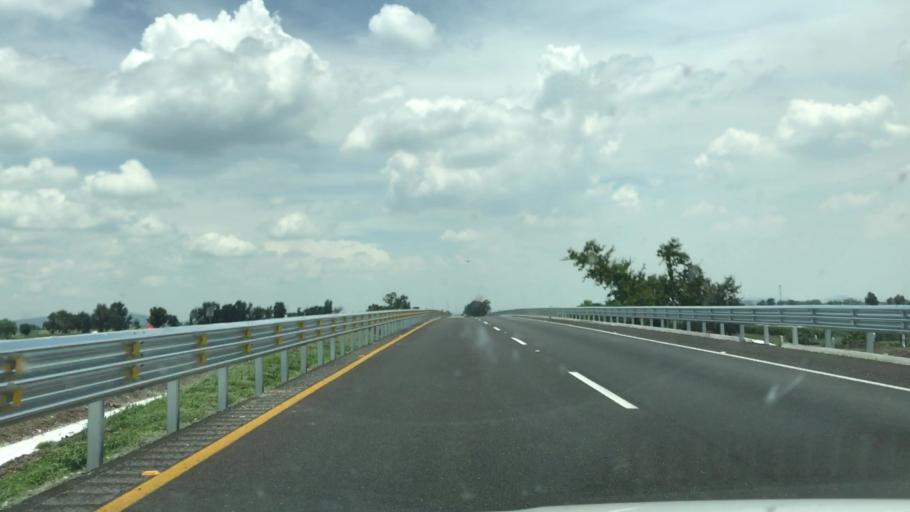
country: MX
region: Guanajuato
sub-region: Salamanca
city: San Vicente de Flores
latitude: 20.6366
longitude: -101.2596
